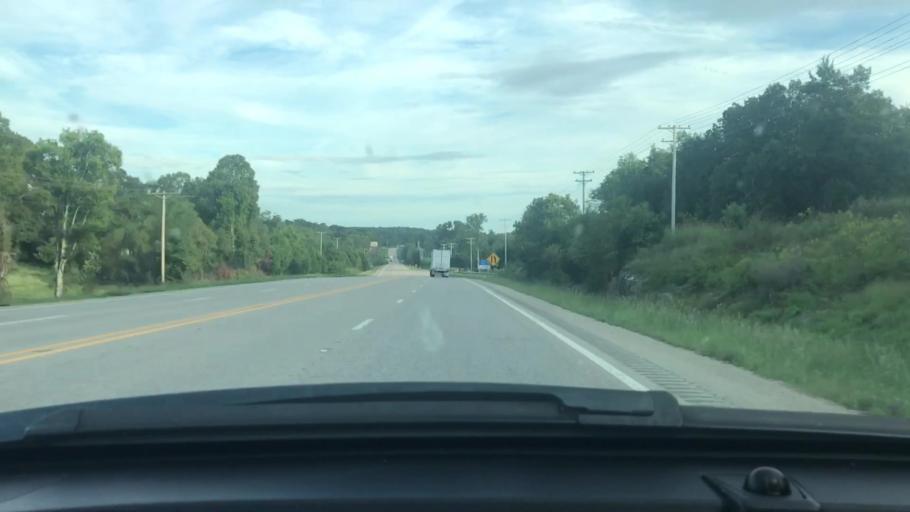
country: US
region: Arkansas
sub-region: Lawrence County
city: Hoxie
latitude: 36.1250
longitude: -91.1539
